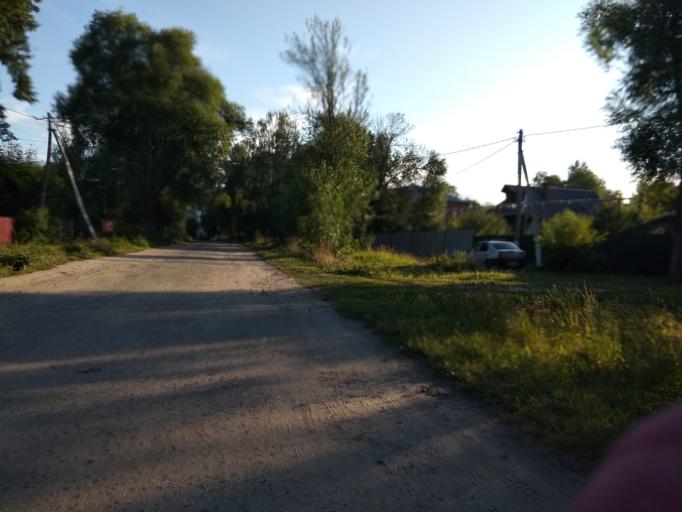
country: RU
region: Moskovskaya
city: Misheronskiy
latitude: 55.7214
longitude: 39.7427
